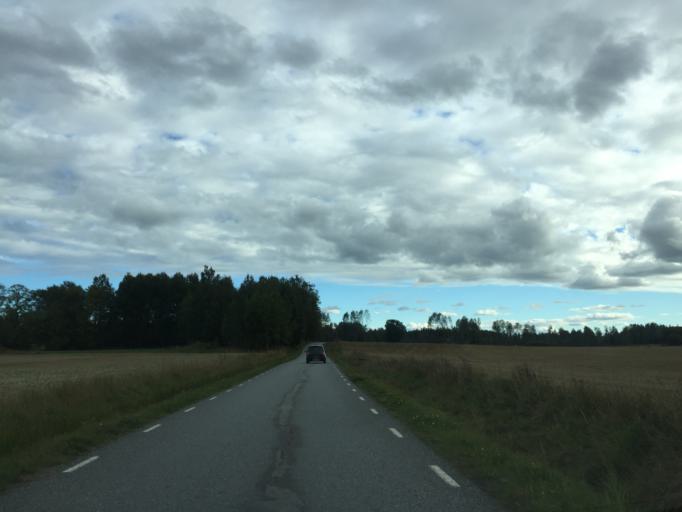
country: SE
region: OErebro
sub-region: Orebro Kommun
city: Hovsta
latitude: 59.3410
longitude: 15.1720
